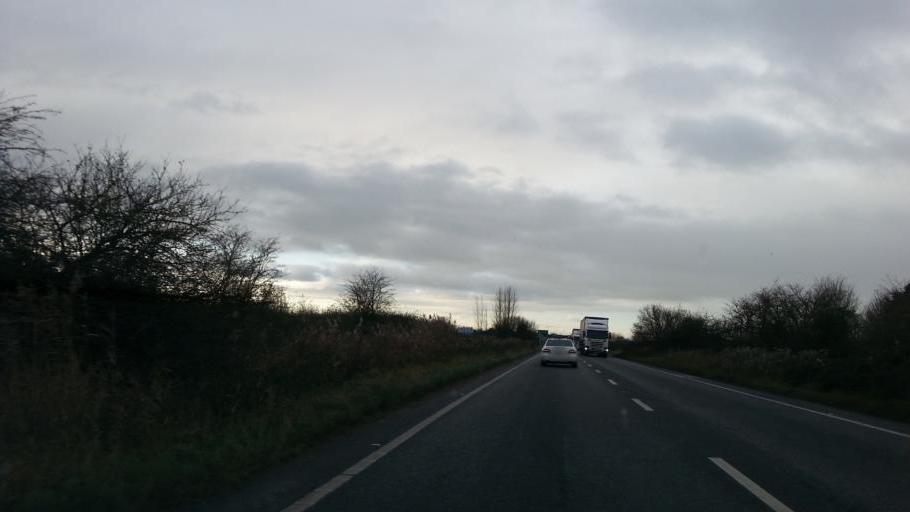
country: GB
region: England
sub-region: Cambridgeshire
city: Wisbech
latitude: 52.6453
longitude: 0.1451
